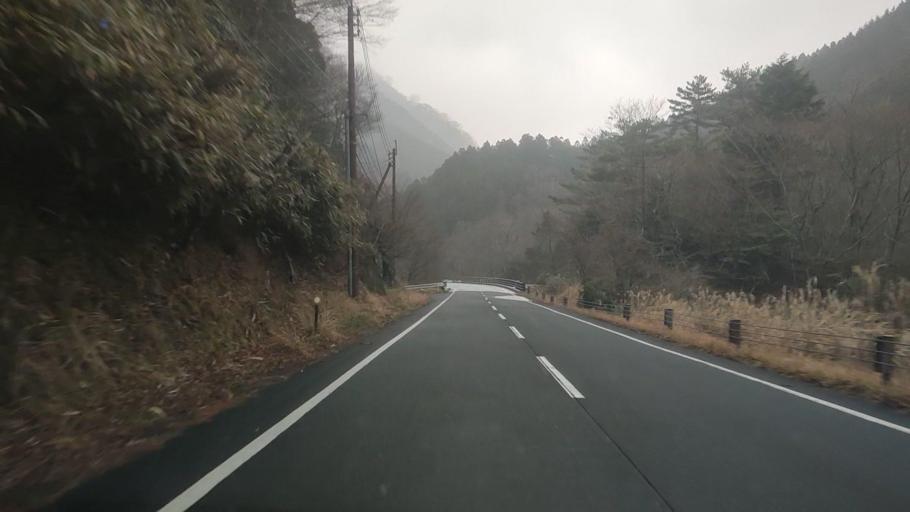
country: JP
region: Kumamoto
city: Matsubase
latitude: 32.5662
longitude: 130.9108
